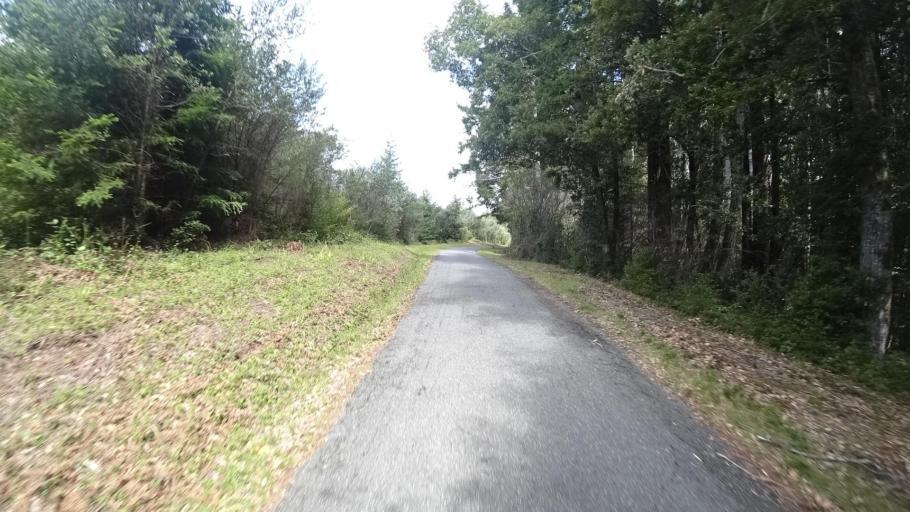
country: US
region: California
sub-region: Humboldt County
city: Blue Lake
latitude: 40.7781
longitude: -123.9624
